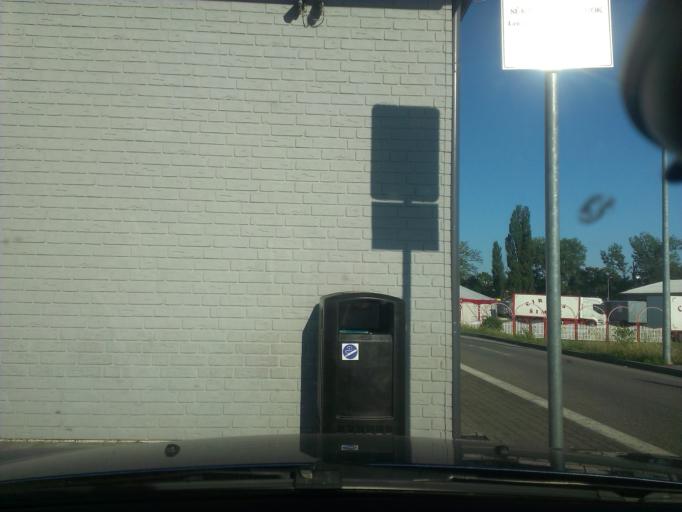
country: SK
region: Trnavsky
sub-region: Okres Trnava
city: Piestany
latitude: 48.5902
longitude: 17.8018
